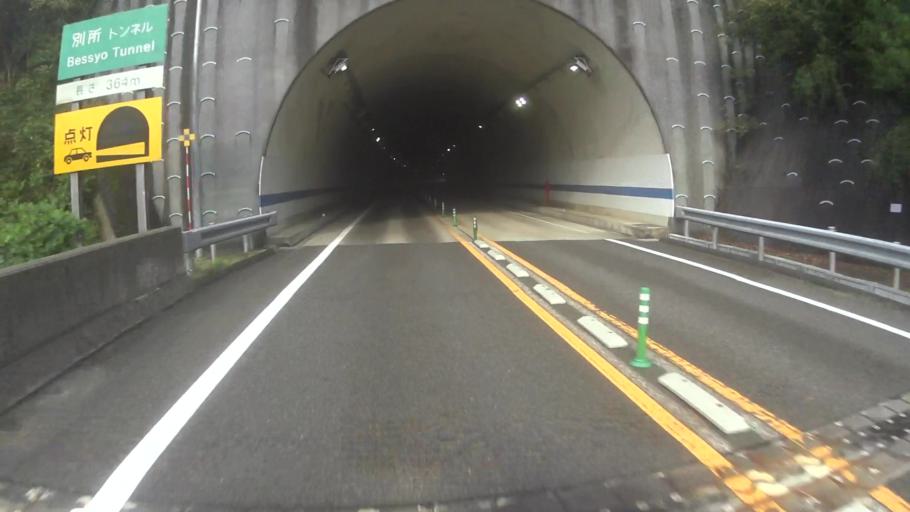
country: JP
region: Kyoto
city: Ayabe
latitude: 35.3754
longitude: 135.2674
